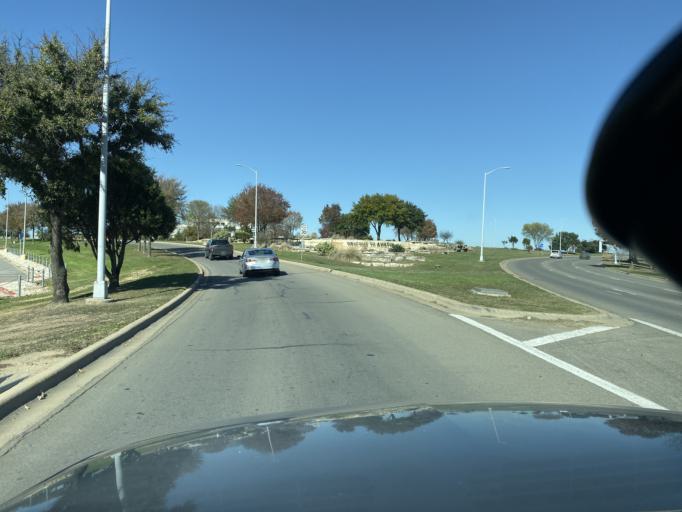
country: US
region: Texas
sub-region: Travis County
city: Hornsby Bend
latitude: 30.2085
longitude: -97.6628
